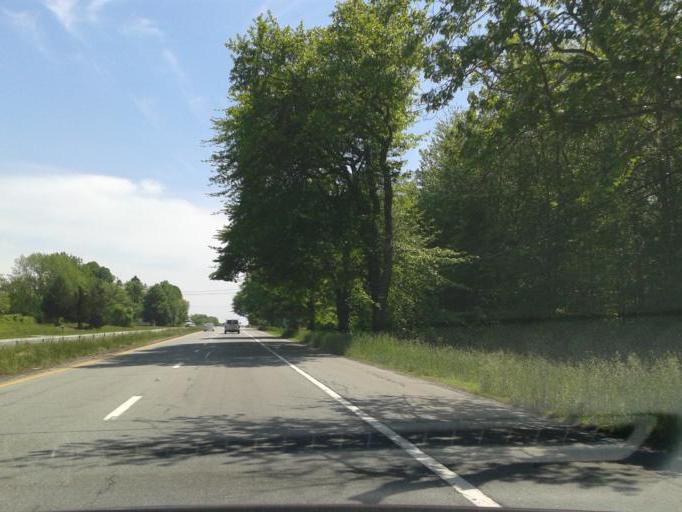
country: US
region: Rhode Island
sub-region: Washington County
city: North Kingstown
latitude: 41.5205
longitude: -71.4624
